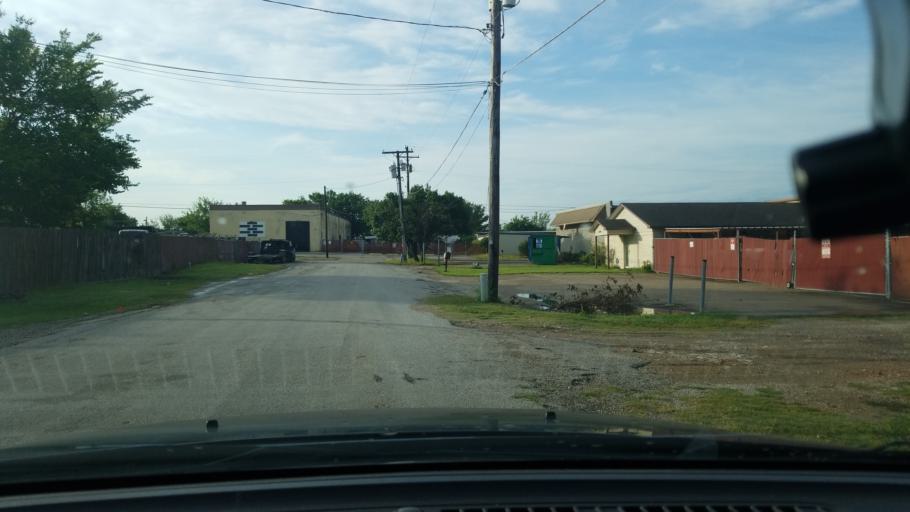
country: US
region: Texas
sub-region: Dallas County
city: Mesquite
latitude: 32.7959
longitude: -96.6188
